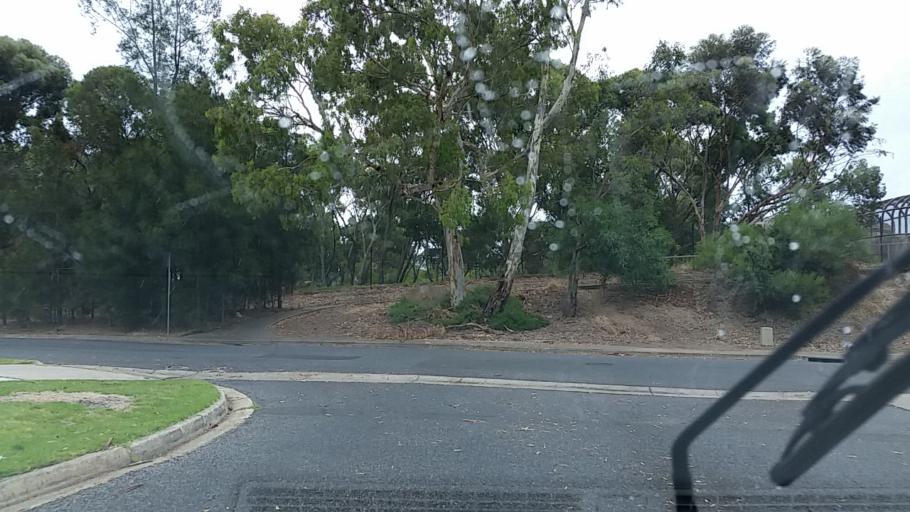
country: AU
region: South Australia
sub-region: Tea Tree Gully
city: Hope Valley
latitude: -34.8375
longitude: 138.6927
